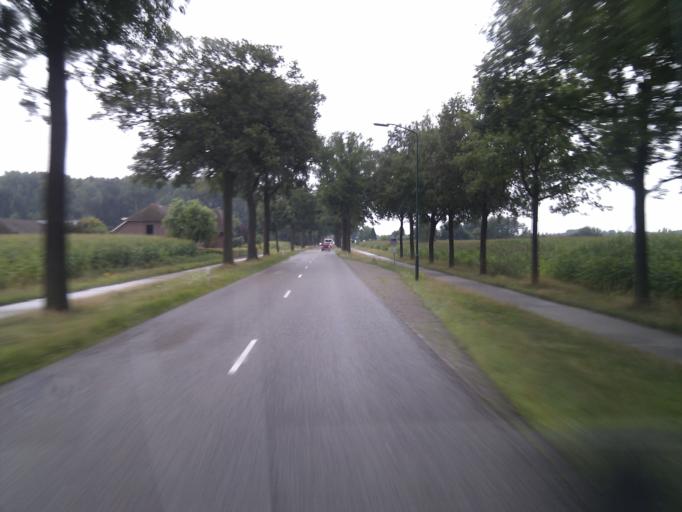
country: NL
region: North Brabant
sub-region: Gemeente Sint-Oedenrode
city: Sint-Oedenrode
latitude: 51.5909
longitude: 5.4560
